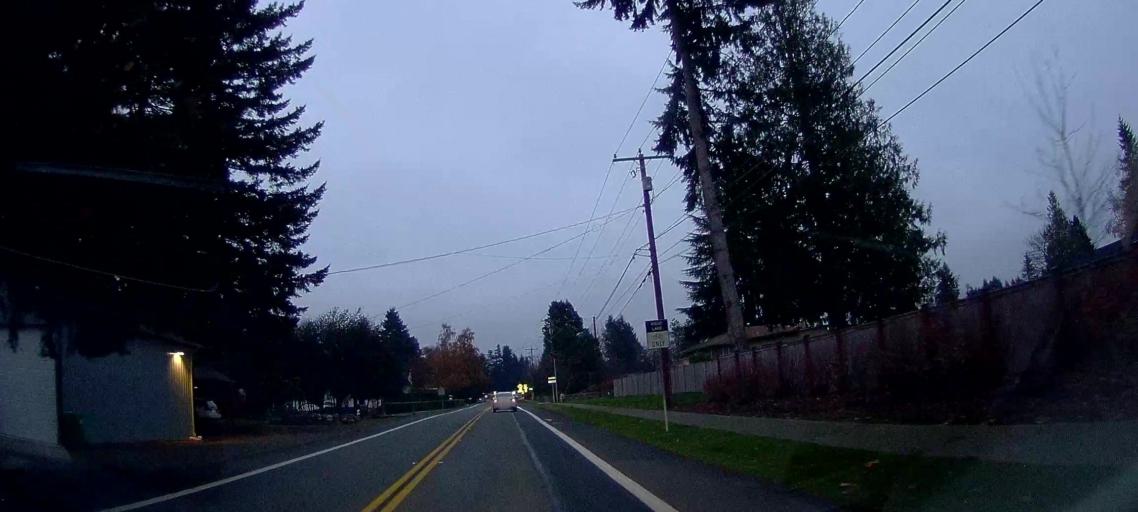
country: US
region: Washington
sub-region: Thurston County
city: Olympia
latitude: 47.0290
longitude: -122.8693
